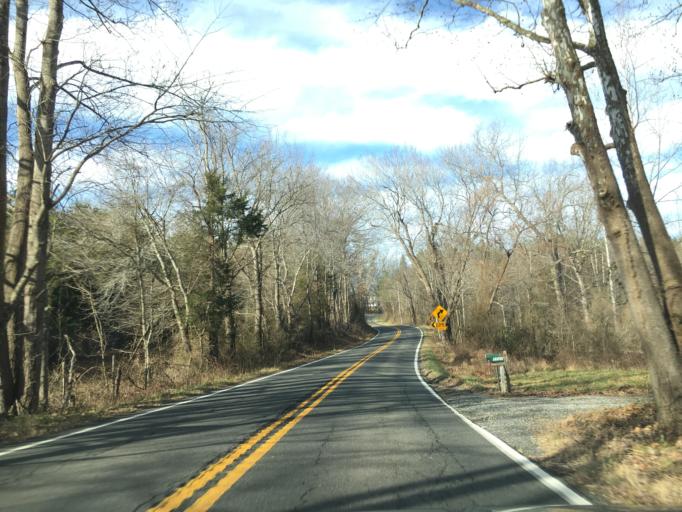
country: US
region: Virginia
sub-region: Fauquier County
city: Warrenton
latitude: 38.7167
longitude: -77.9375
